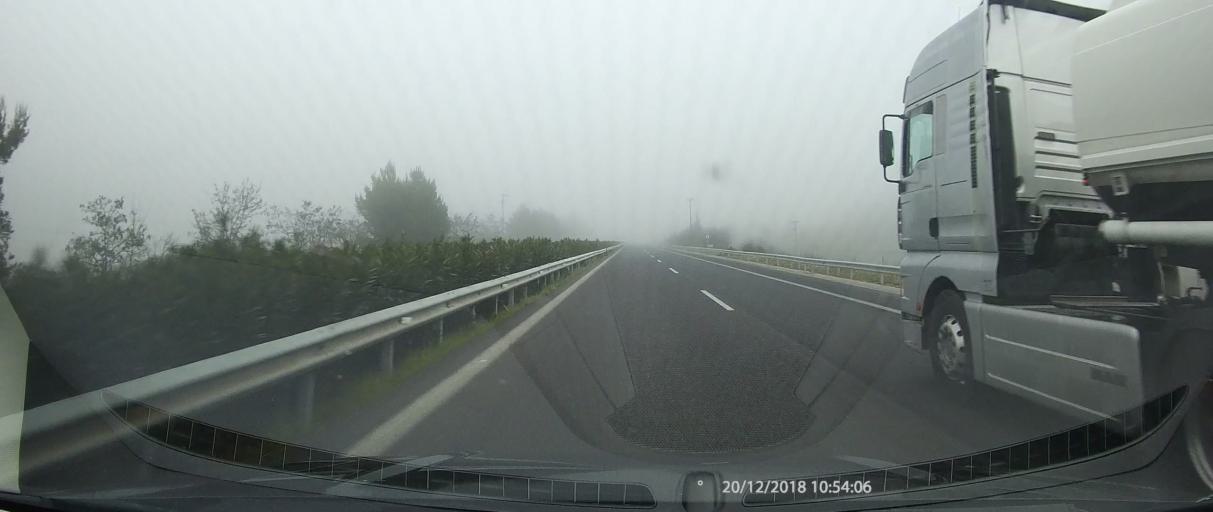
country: GR
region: Peloponnese
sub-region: Nomos Arkadias
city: Tripoli
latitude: 37.6217
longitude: 22.4623
